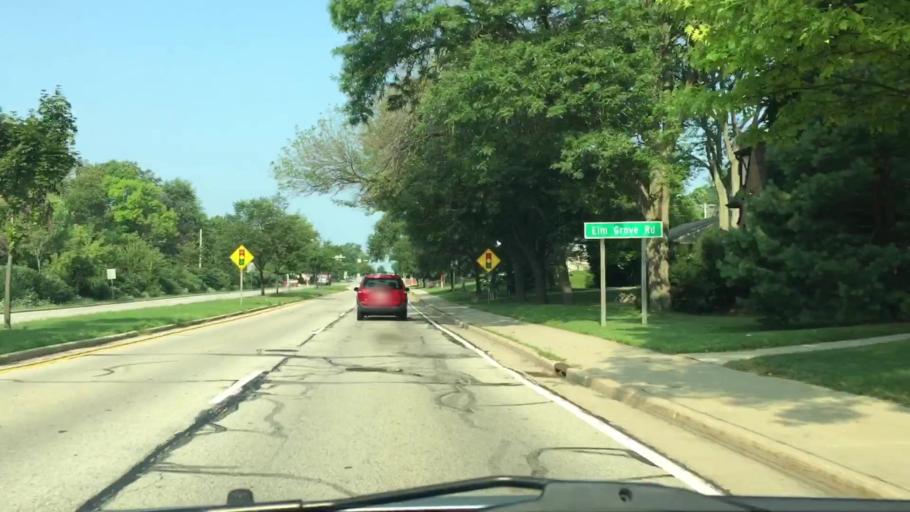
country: US
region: Wisconsin
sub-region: Waukesha County
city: Elm Grove
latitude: 43.0165
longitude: -88.0746
